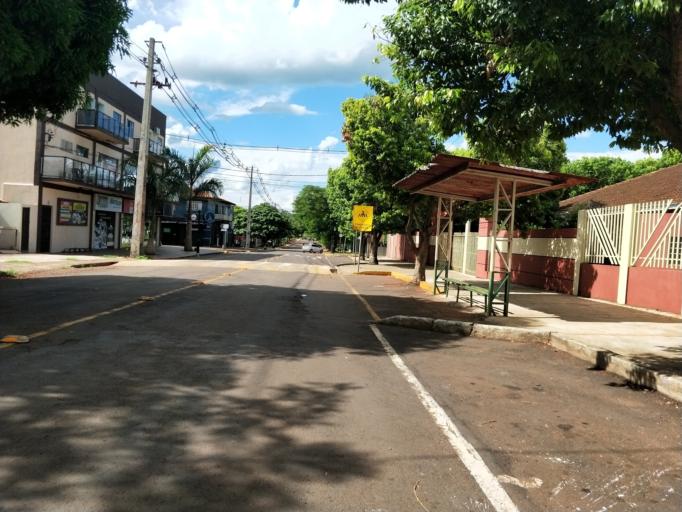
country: BR
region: Parana
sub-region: Marechal Candido Rondon
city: Marechal Candido Rondon
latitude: -24.5583
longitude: -54.0497
